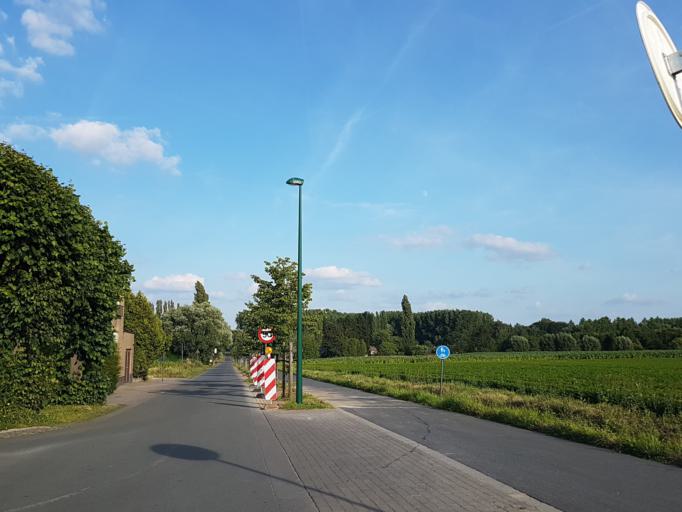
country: BE
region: Flanders
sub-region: Provincie Oost-Vlaanderen
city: Denderleeuw
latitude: 50.9306
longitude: 4.1009
